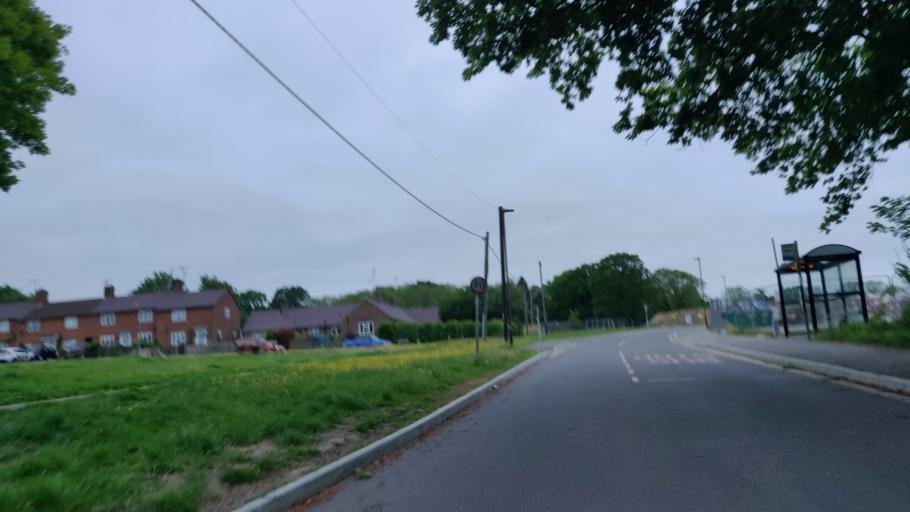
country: GB
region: England
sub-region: West Sussex
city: Southwater
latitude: 51.0242
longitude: -0.3547
